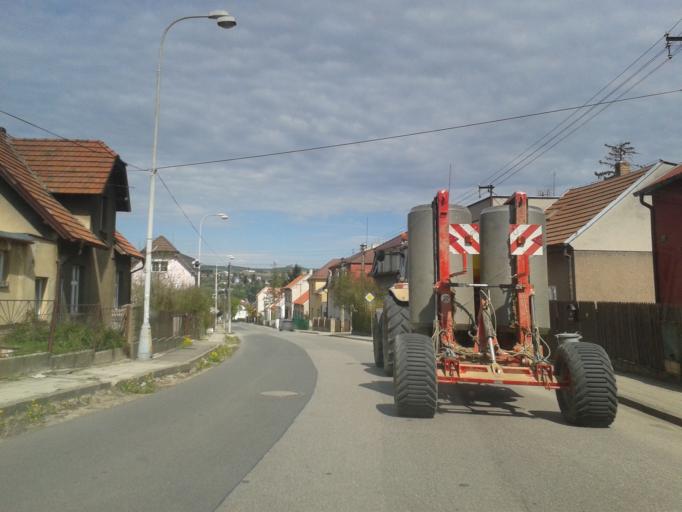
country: CZ
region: Central Bohemia
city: Revnice
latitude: 49.9100
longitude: 14.2301
